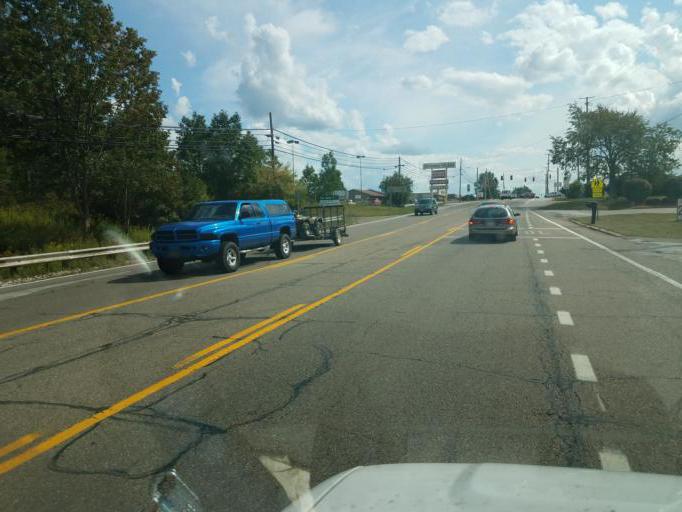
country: US
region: Ohio
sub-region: Portage County
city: Ravenna
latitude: 41.1068
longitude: -81.2425
